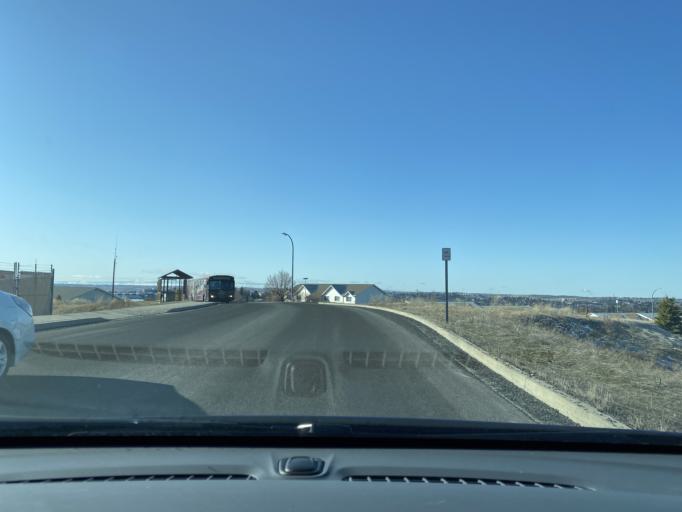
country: US
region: Washington
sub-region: Whitman County
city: Pullman
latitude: 46.7470
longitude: -117.1512
